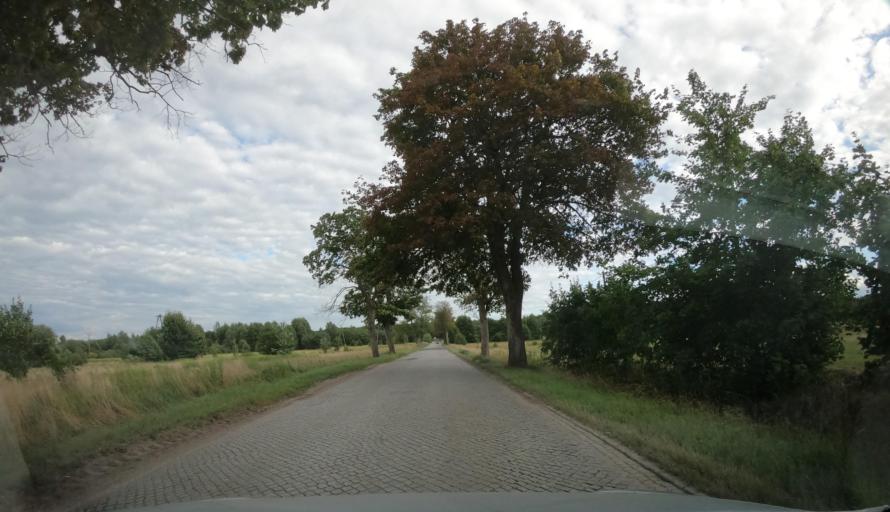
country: PL
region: West Pomeranian Voivodeship
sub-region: Powiat slawienski
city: Slawno
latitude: 54.3452
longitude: 16.6851
